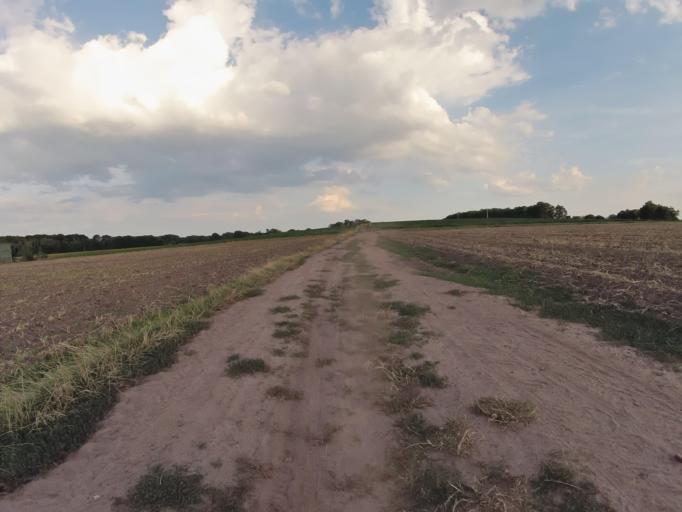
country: DE
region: North Rhine-Westphalia
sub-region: Regierungsbezirk Munster
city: Westerkappeln
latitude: 52.3671
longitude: 7.8795
